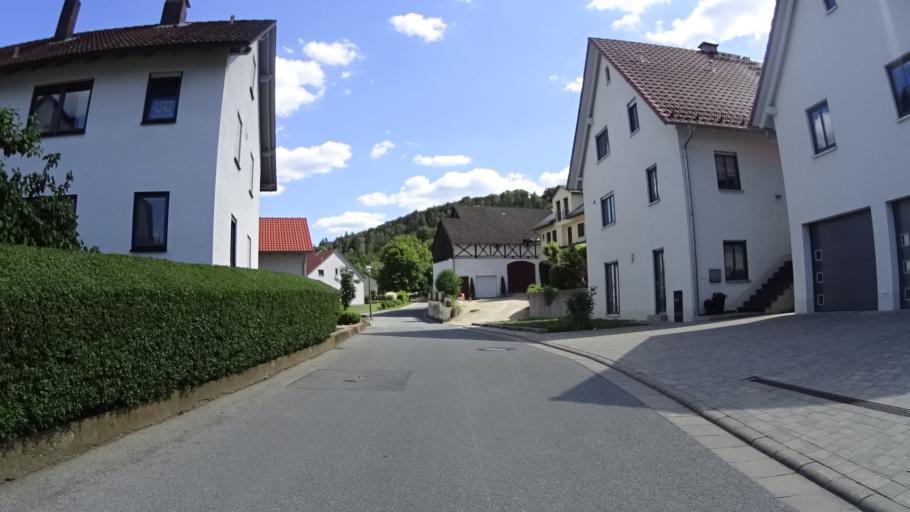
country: DE
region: Bavaria
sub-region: Regierungsbezirk Mittelfranken
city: Greding
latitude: 49.0593
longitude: 11.3208
